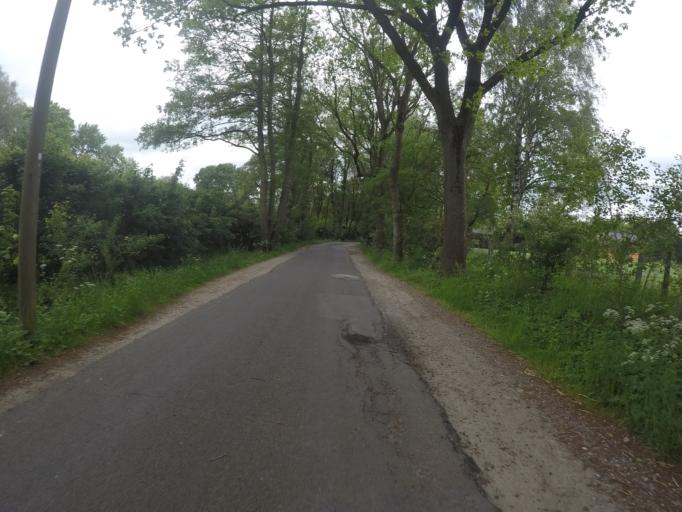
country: DE
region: Schleswig-Holstein
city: Bonningstedt
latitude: 53.6542
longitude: 9.9396
